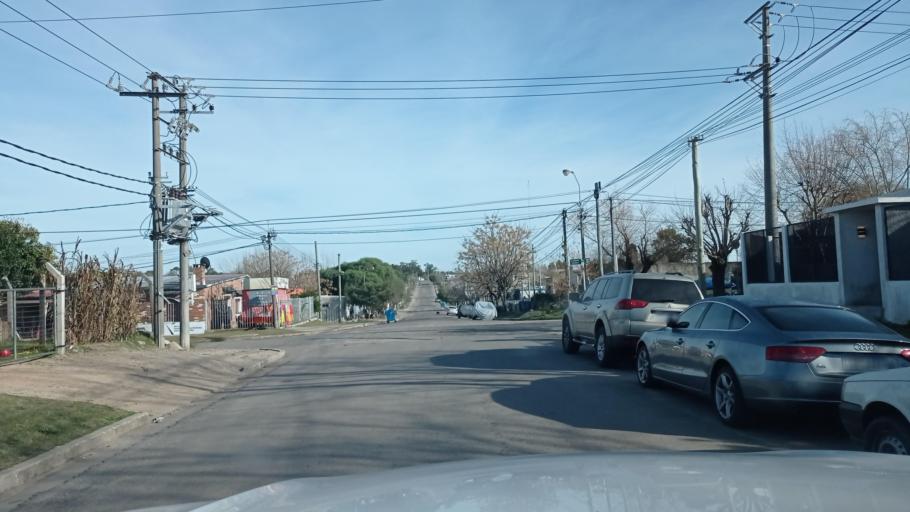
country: UY
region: Florida
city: Florida
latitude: -34.0895
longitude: -56.2332
